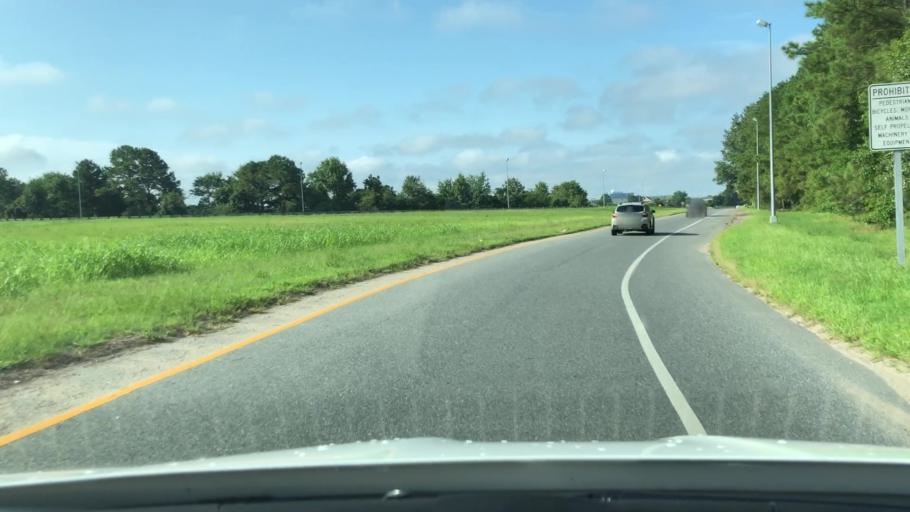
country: US
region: Virginia
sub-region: City of Chesapeake
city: Chesapeake
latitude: 36.7871
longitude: -76.2354
